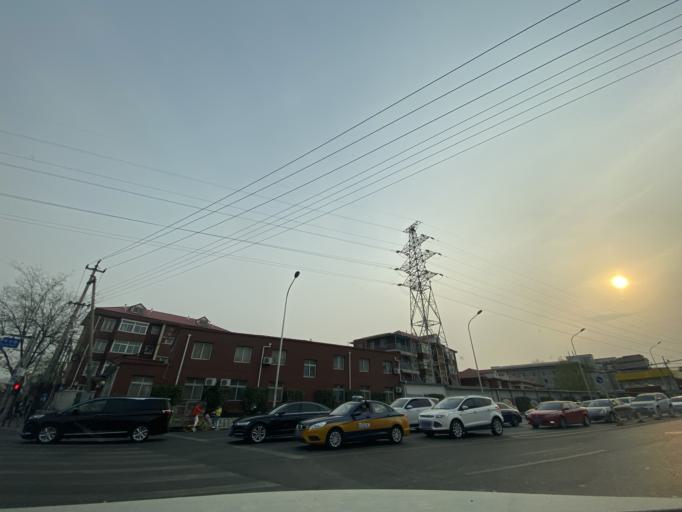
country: CN
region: Beijing
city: Sijiqing
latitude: 39.9272
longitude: 116.2688
